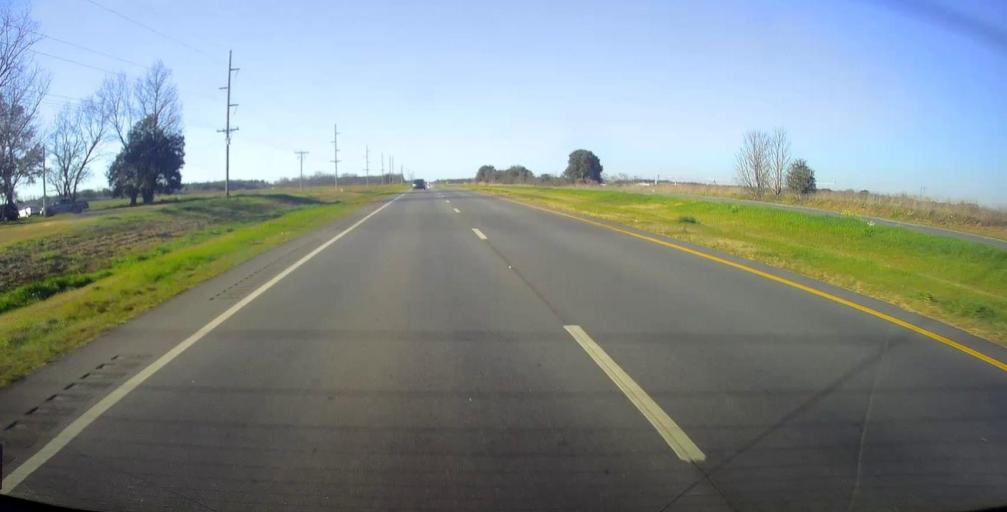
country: US
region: Georgia
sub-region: Lee County
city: Leesburg
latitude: 31.7742
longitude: -84.1922
